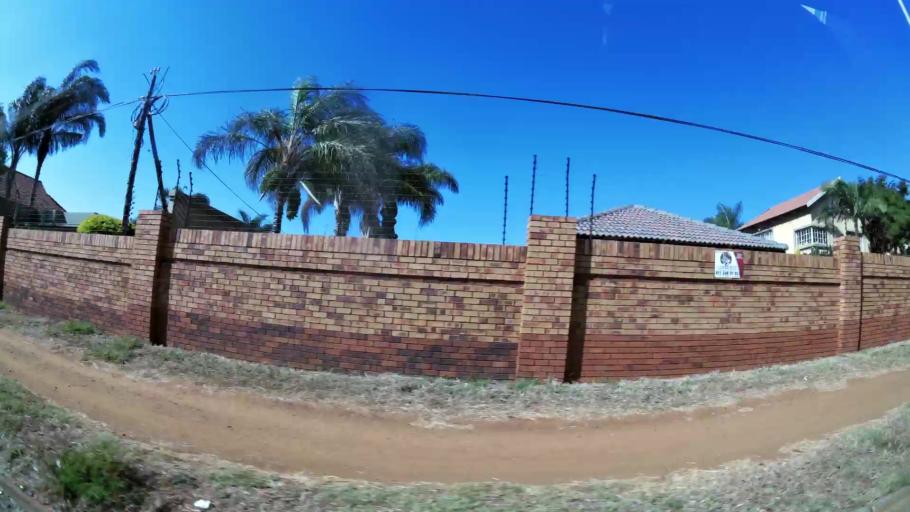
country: ZA
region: Gauteng
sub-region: City of Tshwane Metropolitan Municipality
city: Pretoria
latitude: -25.6660
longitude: 28.2555
